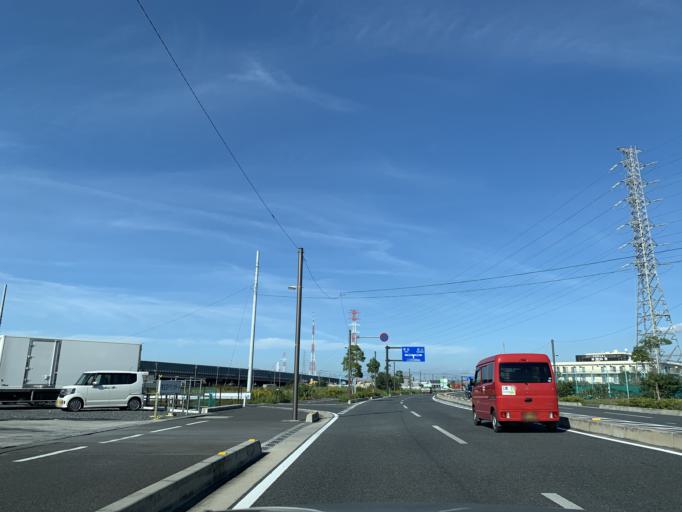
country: JP
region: Chiba
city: Nagareyama
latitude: 35.8435
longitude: 139.8732
